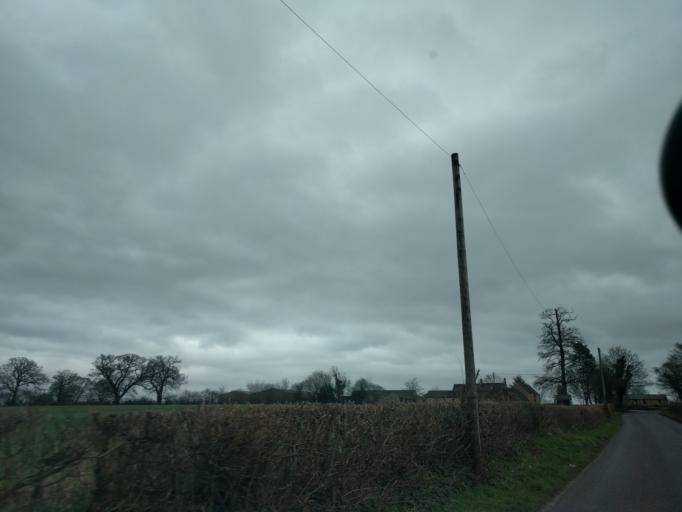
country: GB
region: England
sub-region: Wiltshire
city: Biddestone
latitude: 51.5014
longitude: -2.1959
